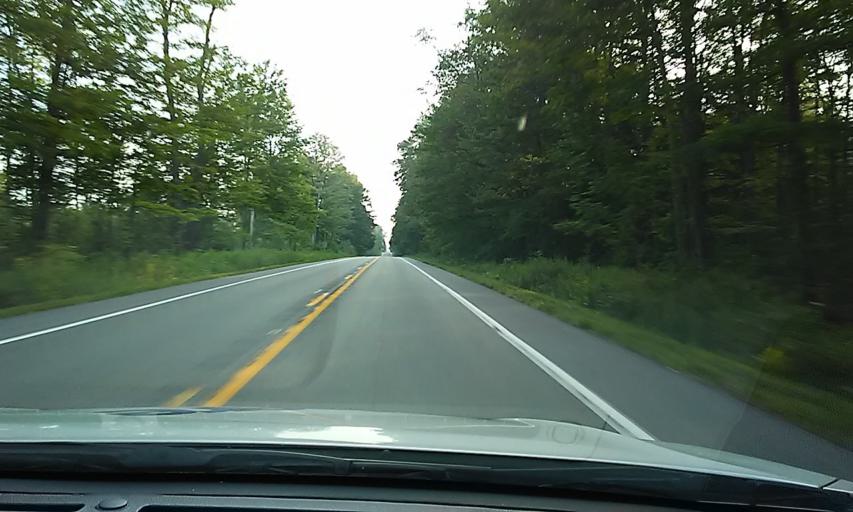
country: US
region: Pennsylvania
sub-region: Warren County
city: Sheffield
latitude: 41.5736
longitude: -78.9672
